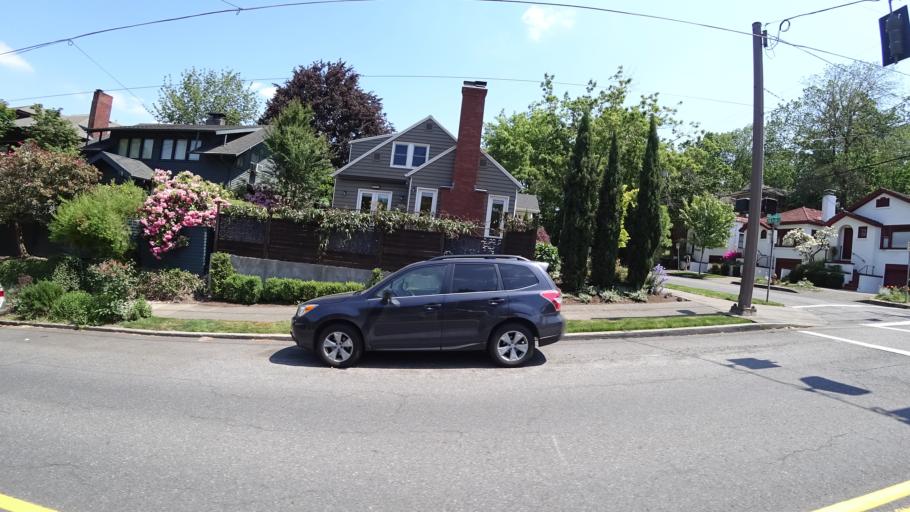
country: US
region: Oregon
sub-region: Multnomah County
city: Portland
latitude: 45.5101
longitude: -122.6987
